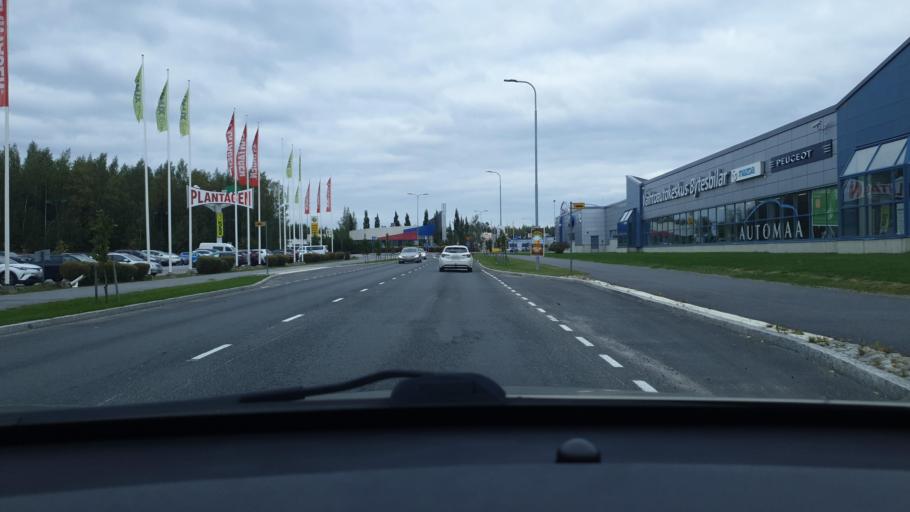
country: FI
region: Ostrobothnia
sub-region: Vaasa
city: Vaasa
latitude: 63.1074
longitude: 21.6481
